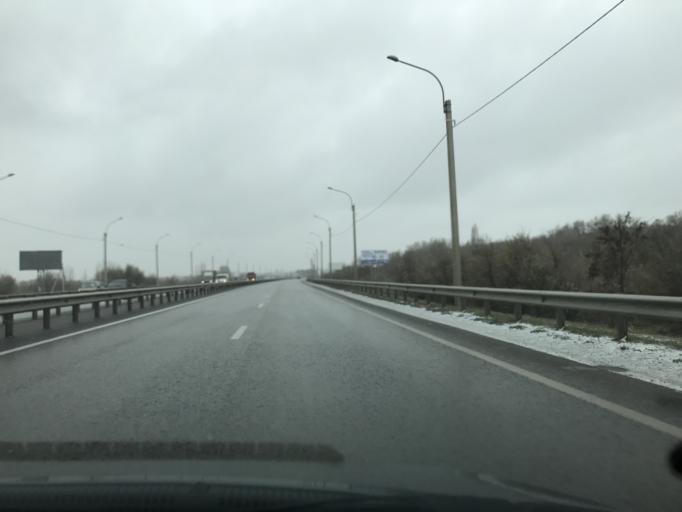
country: RU
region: Rostov
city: Bataysk
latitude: 47.1463
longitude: 39.7747
